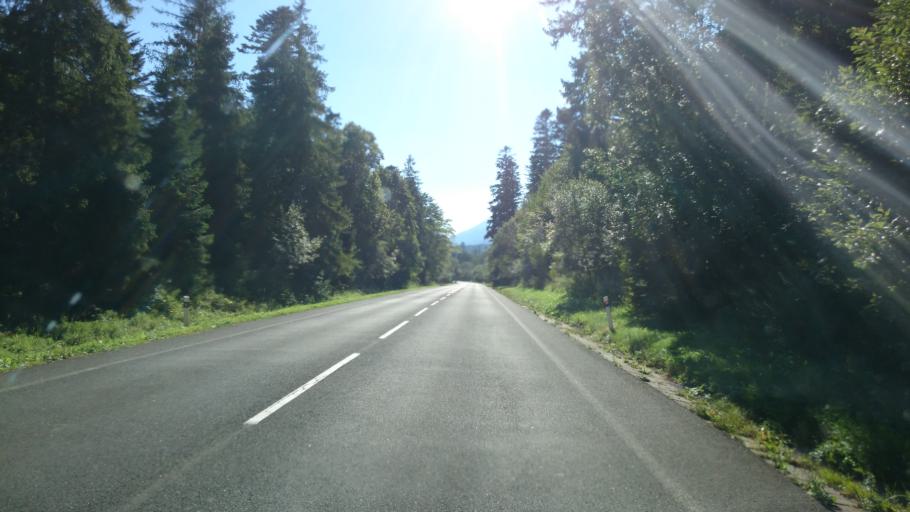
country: SK
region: Presovsky
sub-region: Okres Poprad
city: Zdiar
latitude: 49.2089
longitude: 20.3144
